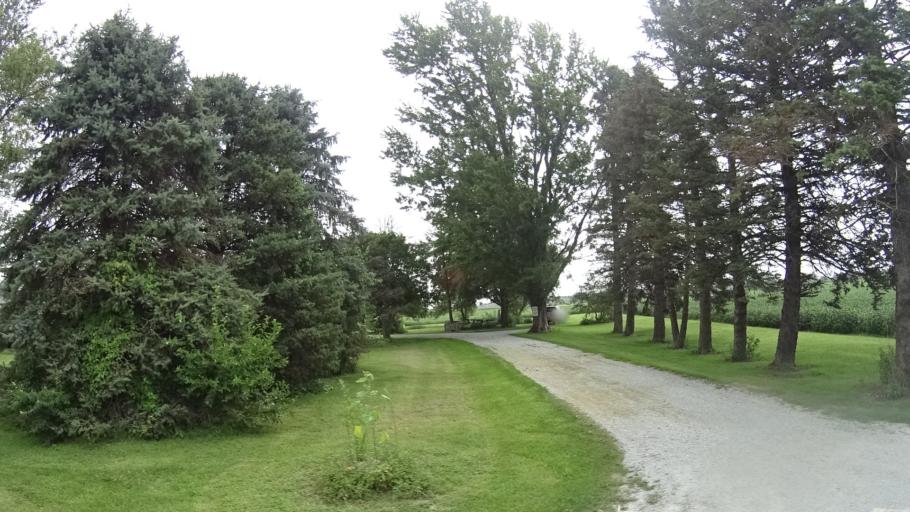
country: US
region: Indiana
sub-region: Madison County
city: Pendleton
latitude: 40.0202
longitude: -85.8055
